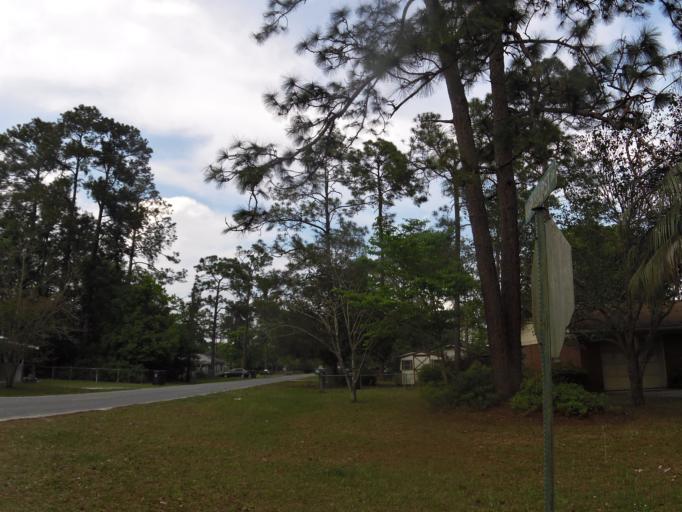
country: US
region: Georgia
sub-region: Charlton County
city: Folkston
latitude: 30.8327
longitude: -81.9851
